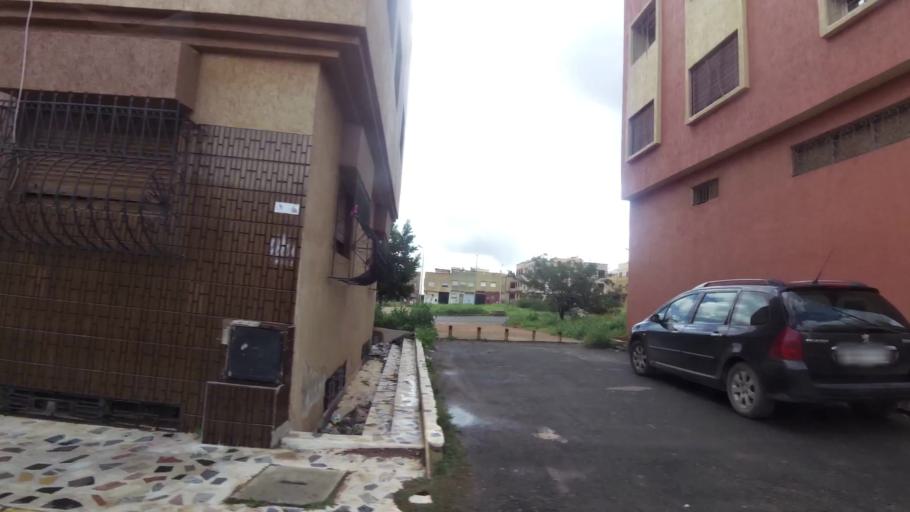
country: MA
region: Grand Casablanca
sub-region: Nouaceur
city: Bouskoura
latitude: 33.5067
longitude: -7.6508
